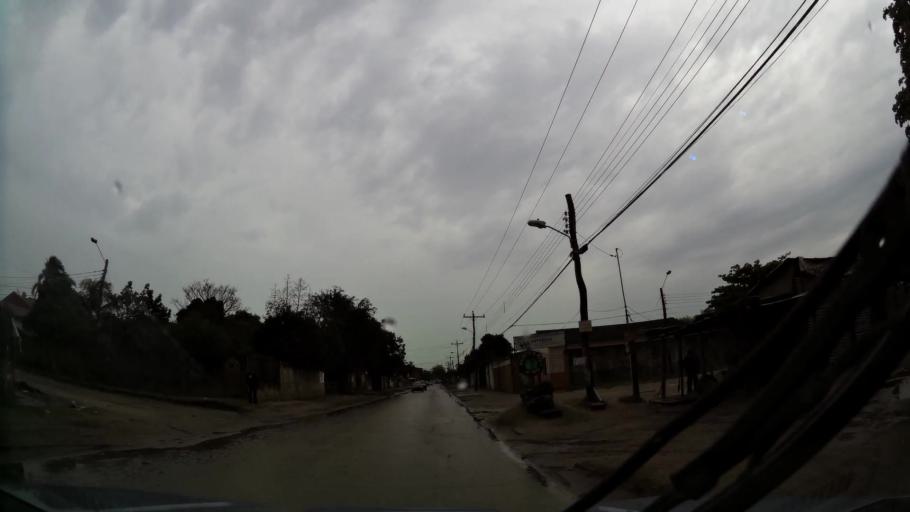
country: BO
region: Santa Cruz
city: Santa Cruz de la Sierra
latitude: -17.7611
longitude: -63.1151
